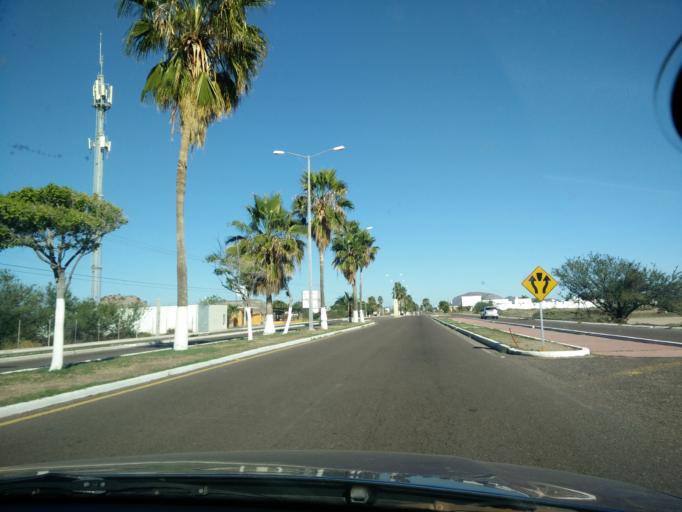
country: MX
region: Sonora
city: Heroica Guaymas
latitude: 27.9647
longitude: -111.0189
